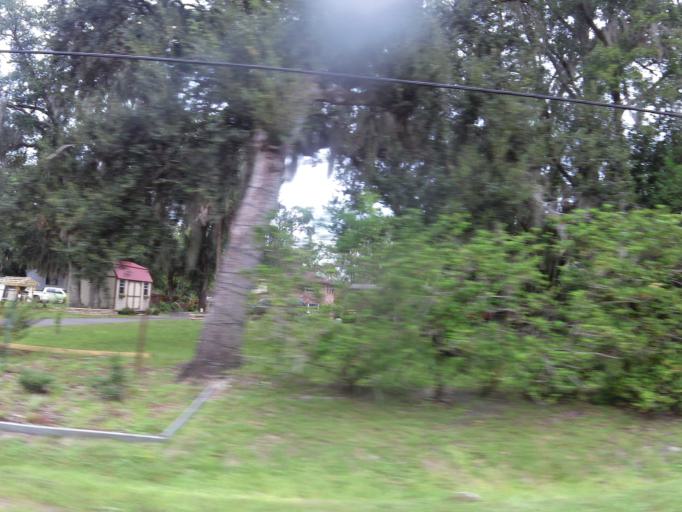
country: US
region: Florida
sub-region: Clay County
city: Bellair-Meadowbrook Terrace
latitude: 30.2561
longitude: -81.7283
